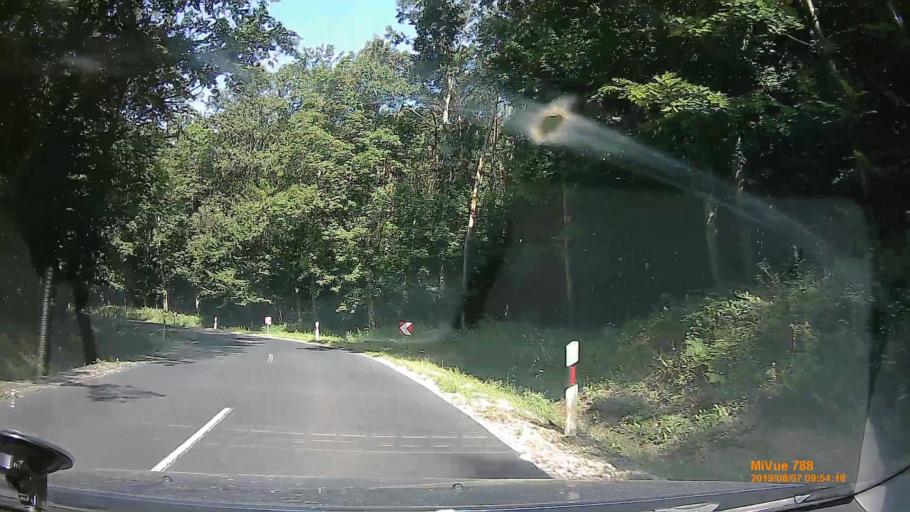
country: HU
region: Zala
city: Zalaegerszeg
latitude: 46.7337
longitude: 16.8715
